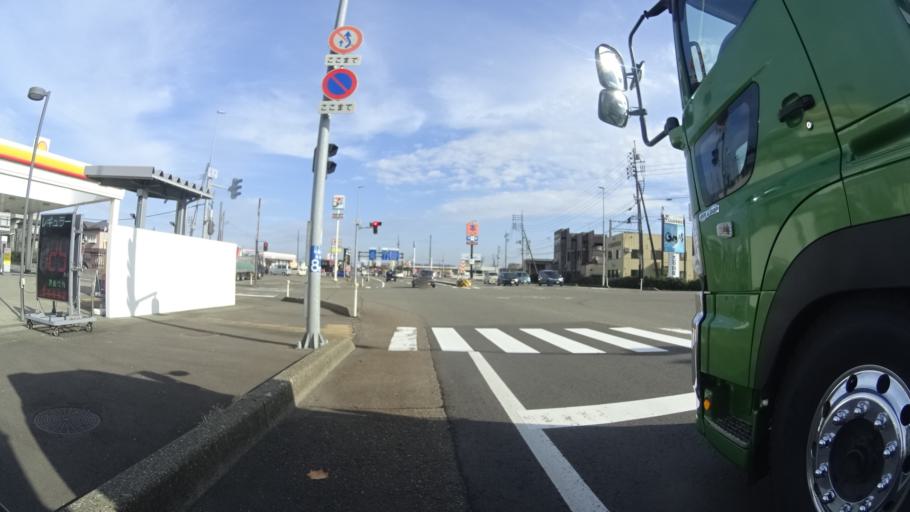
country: JP
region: Niigata
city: Joetsu
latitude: 37.1592
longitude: 138.2252
